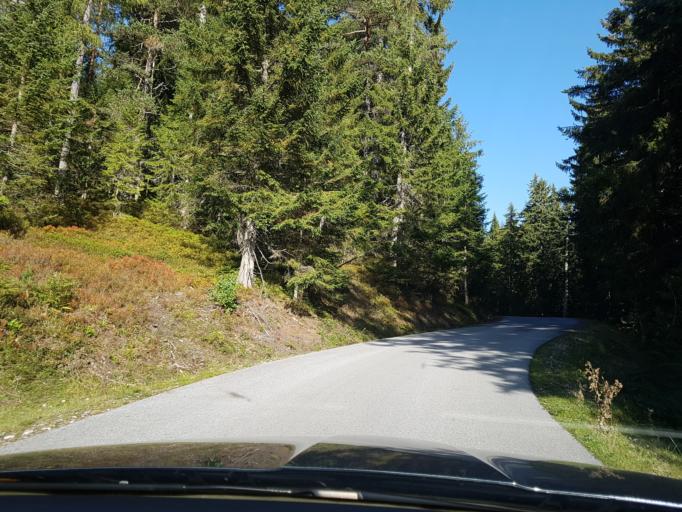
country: AT
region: Salzburg
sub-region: Politischer Bezirk Sankt Johann im Pongau
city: Filzmoos
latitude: 47.4074
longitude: 13.5081
